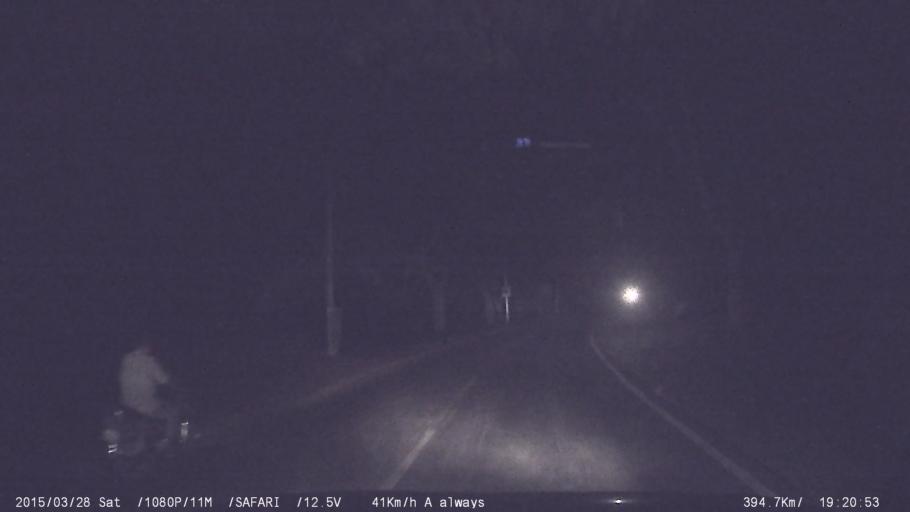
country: IN
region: Karnataka
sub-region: Mandya
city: Shrirangapattana
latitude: 12.4175
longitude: 76.6618
